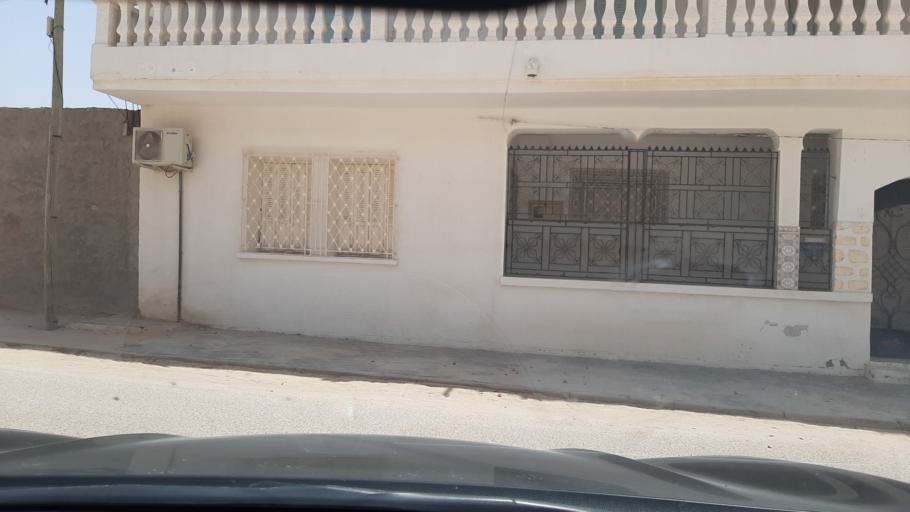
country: TN
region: Qabis
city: Matmata
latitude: 33.6167
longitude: 10.2809
